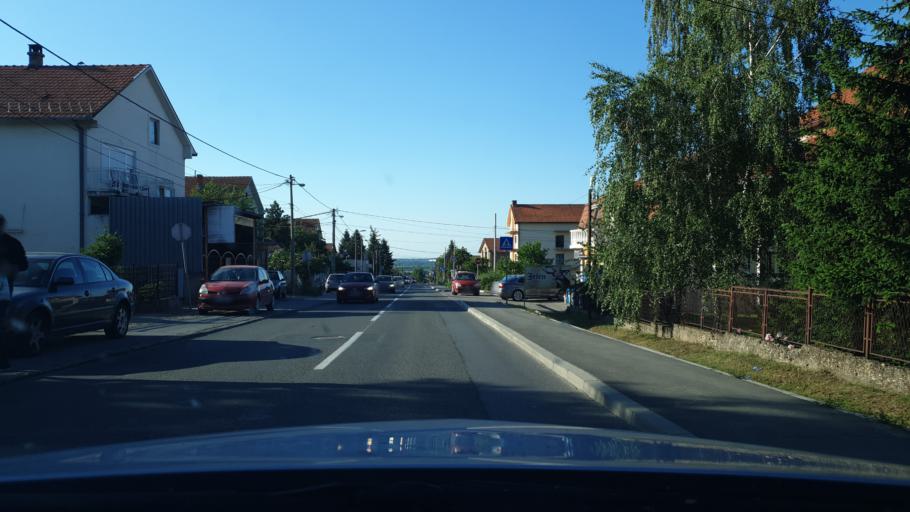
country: RS
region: Central Serbia
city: Sremcica
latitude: 44.7158
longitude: 20.3683
